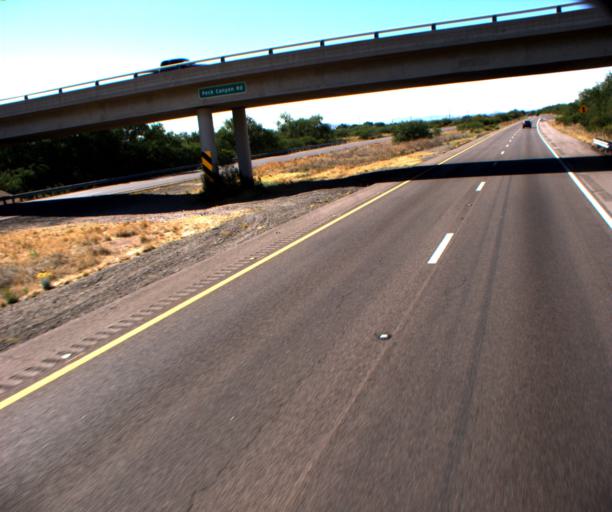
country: US
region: Arizona
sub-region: Santa Cruz County
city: Rio Rico
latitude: 31.5065
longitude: -111.0119
